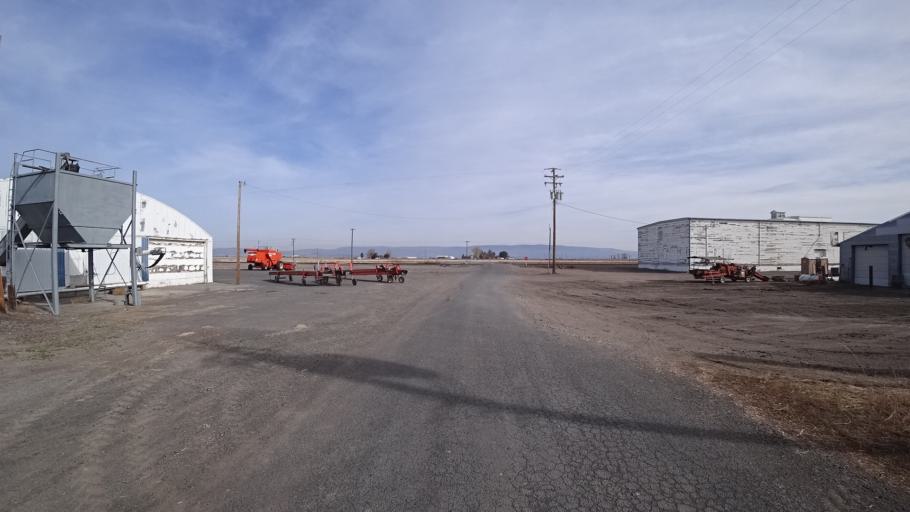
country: US
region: California
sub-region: Siskiyou County
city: Tulelake
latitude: 41.9498
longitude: -121.4676
